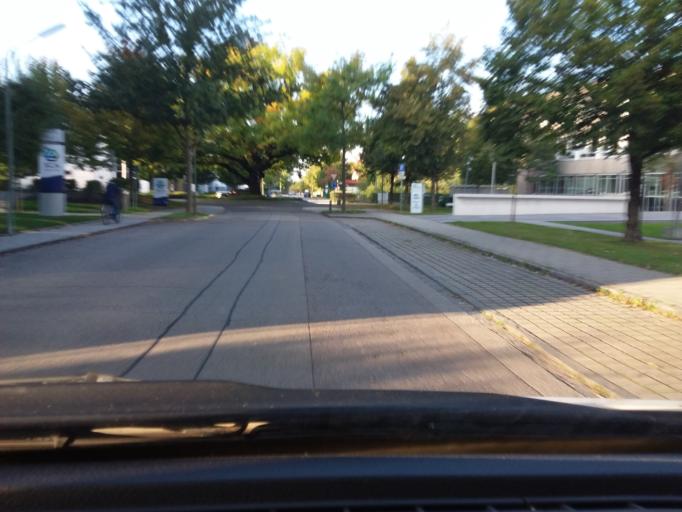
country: DE
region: Bavaria
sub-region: Upper Bavaria
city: Ismaning
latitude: 48.2297
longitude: 11.6837
